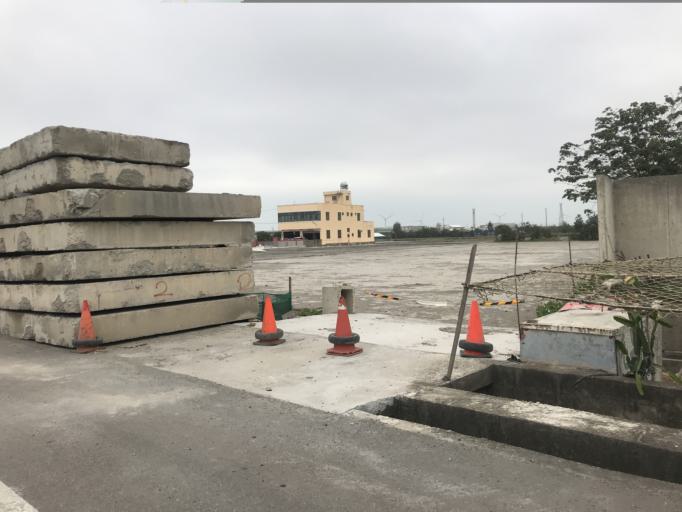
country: TW
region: Taiwan
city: Fengyuan
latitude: 24.3758
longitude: 120.5956
